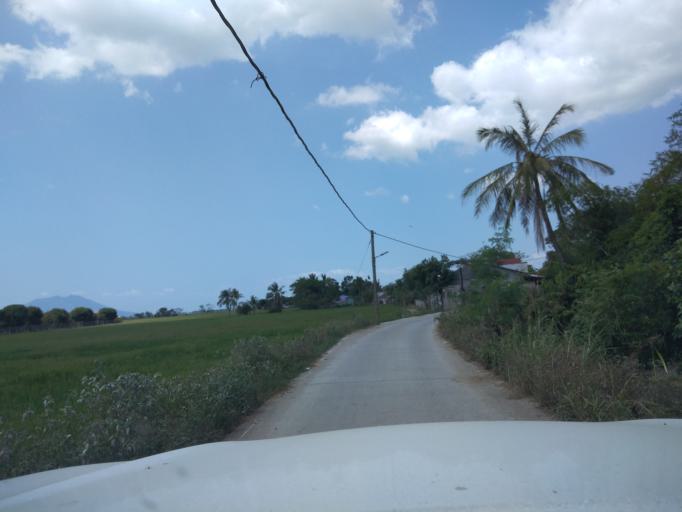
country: PH
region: Central Luzon
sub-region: Province of Pampanga
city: Bahay Pare
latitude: 15.0362
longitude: 120.8718
